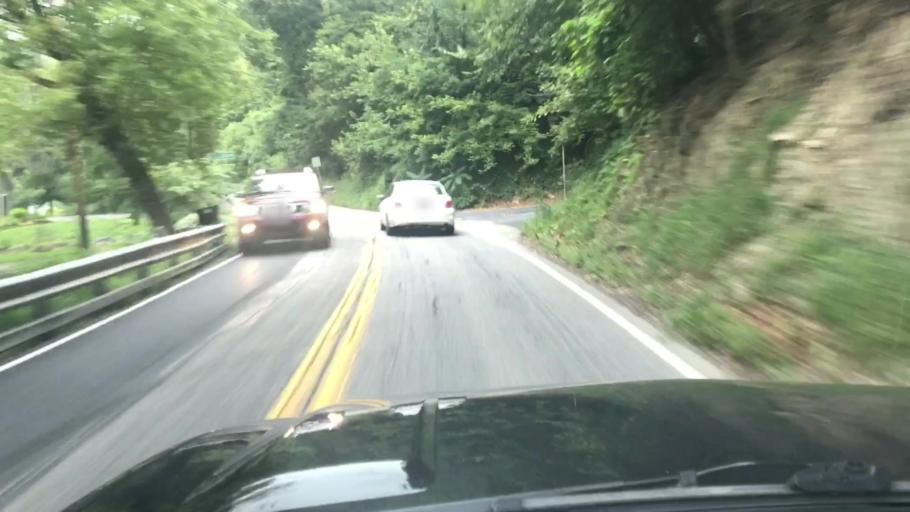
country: US
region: Pennsylvania
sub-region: Cumberland County
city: Shiremanstown
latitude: 40.2579
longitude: -76.9760
